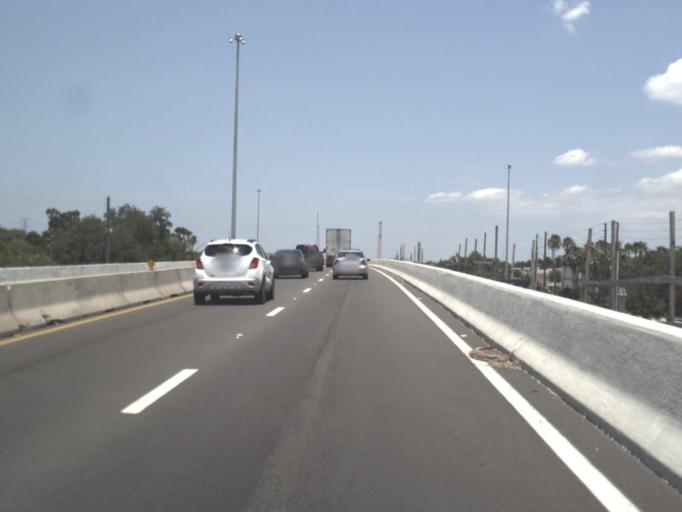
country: US
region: Florida
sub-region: Pinellas County
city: South Highpoint
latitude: 27.9533
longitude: -82.7301
